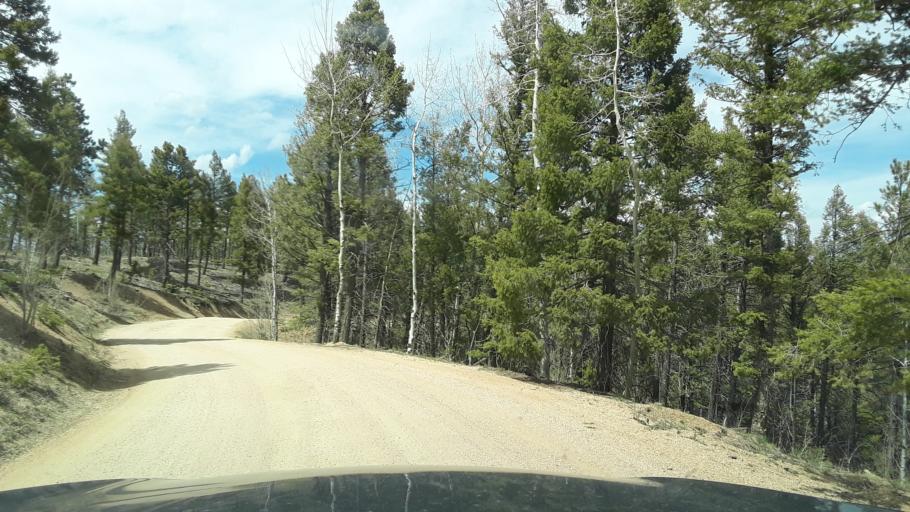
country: US
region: Colorado
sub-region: El Paso County
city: Palmer Lake
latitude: 39.0599
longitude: -104.9743
